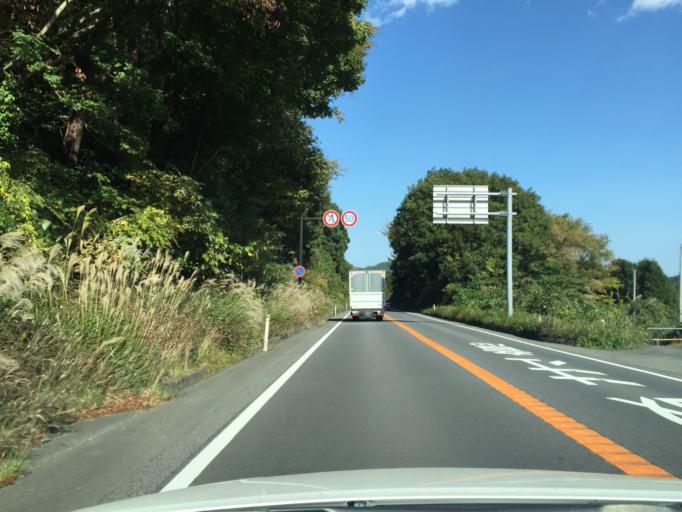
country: JP
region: Fukushima
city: Iwaki
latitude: 37.0763
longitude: 140.7951
